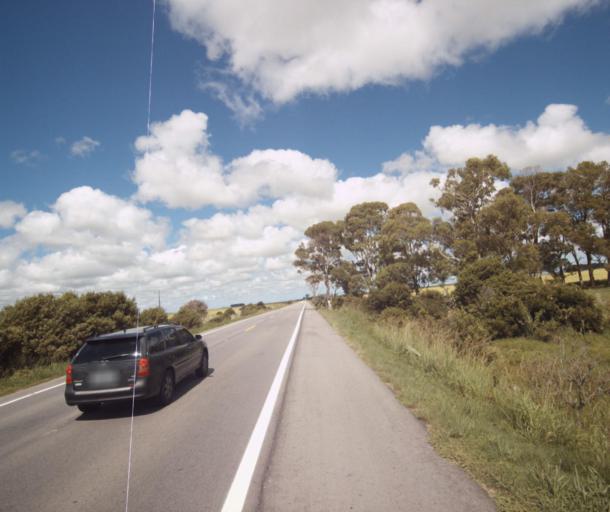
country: BR
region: Rio Grande do Sul
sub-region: Rio Grande
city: Rio Grande
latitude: -32.1633
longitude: -52.4047
